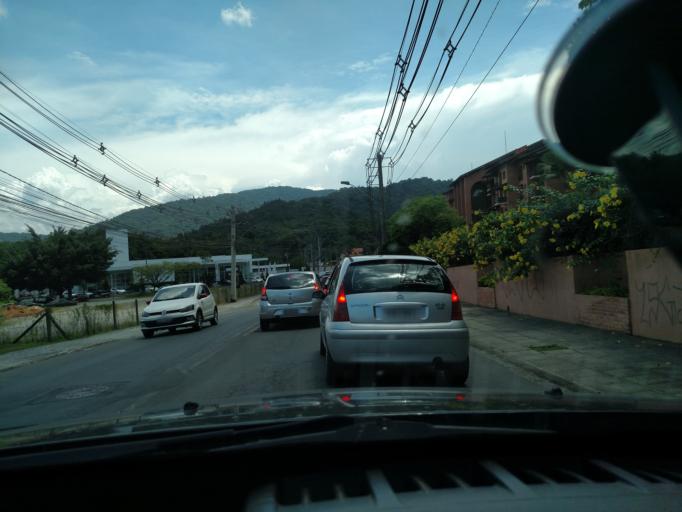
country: BR
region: Santa Catarina
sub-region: Blumenau
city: Blumenau
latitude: -26.9351
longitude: -49.0662
